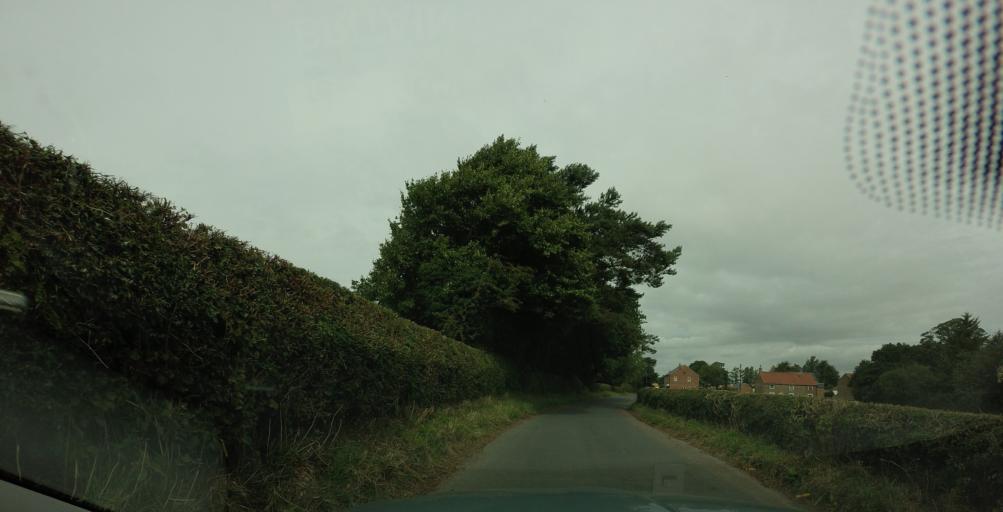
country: GB
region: England
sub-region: North Yorkshire
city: Ripon
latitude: 54.1346
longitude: -1.4839
